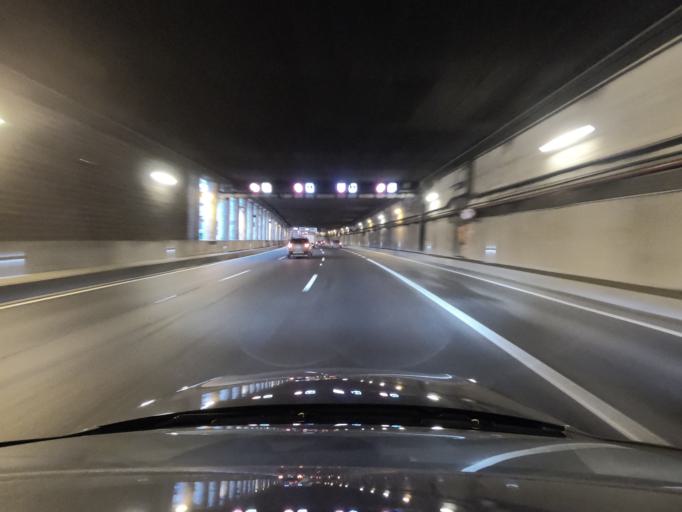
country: PT
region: Lisbon
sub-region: Amadora
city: Amadora
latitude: 38.7505
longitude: -9.2108
